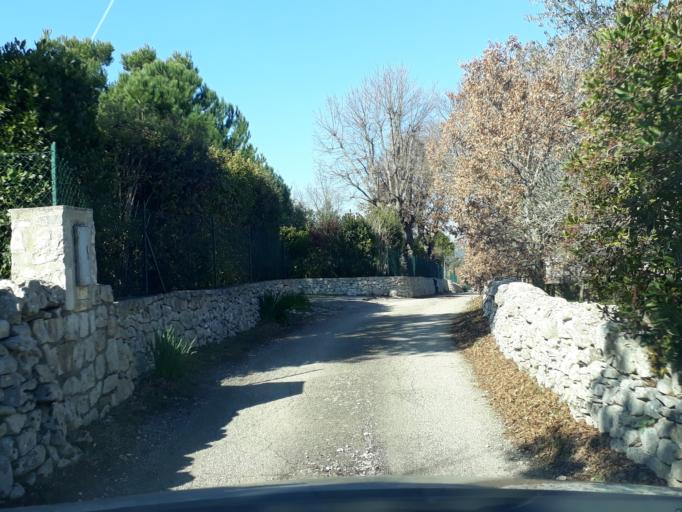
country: IT
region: Apulia
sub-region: Provincia di Brindisi
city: Lamie di Olimpie-Selva
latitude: 40.7981
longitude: 17.3461
